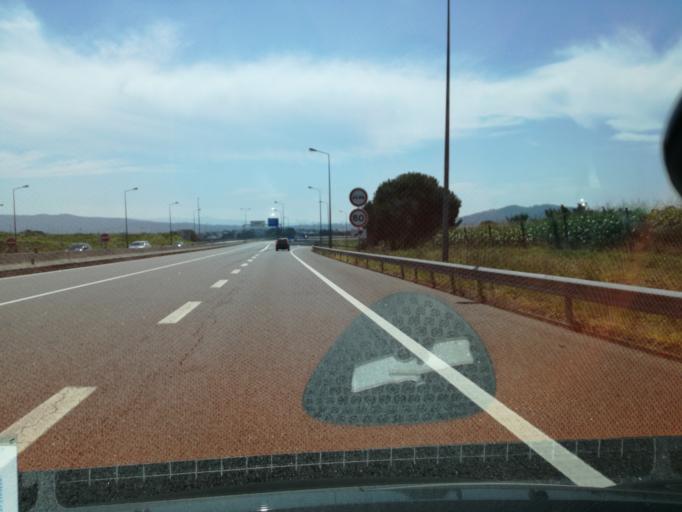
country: PT
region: Viana do Castelo
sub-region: Viana do Castelo
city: Meadela
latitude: 41.7178
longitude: -8.7972
